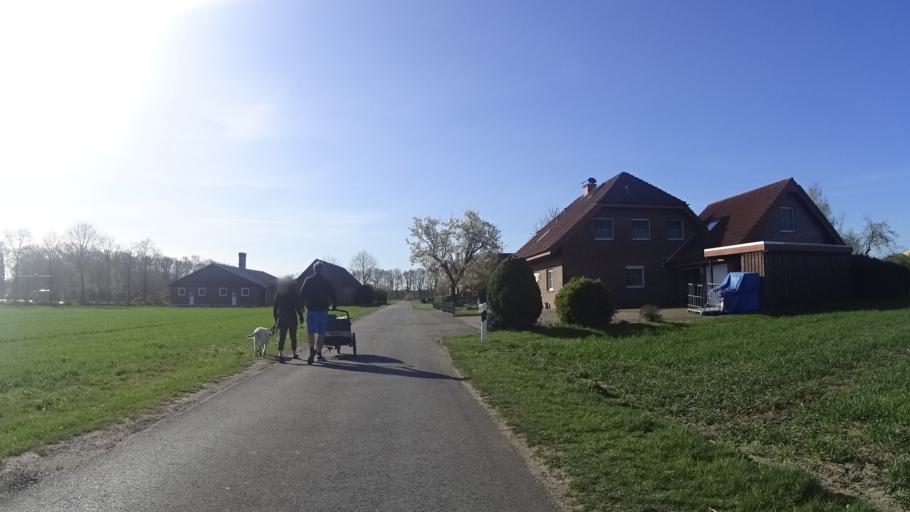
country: DE
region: North Rhine-Westphalia
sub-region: Regierungsbezirk Munster
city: Greven
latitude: 52.0401
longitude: 7.6248
